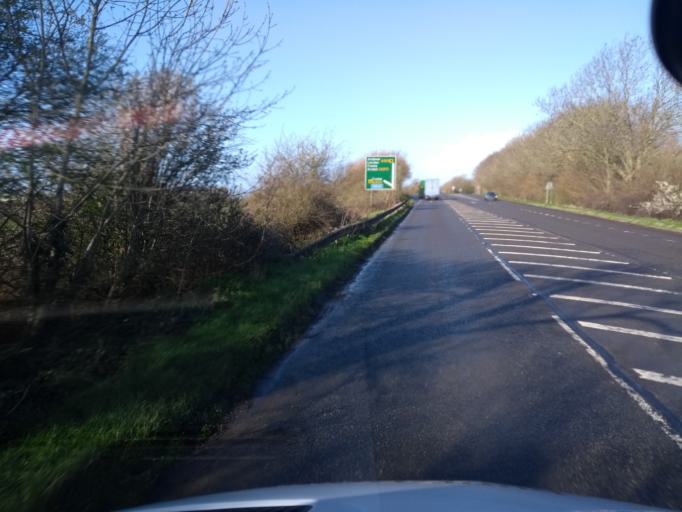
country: GB
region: England
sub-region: Somerset
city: Ilchester
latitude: 50.9995
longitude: -2.6882
